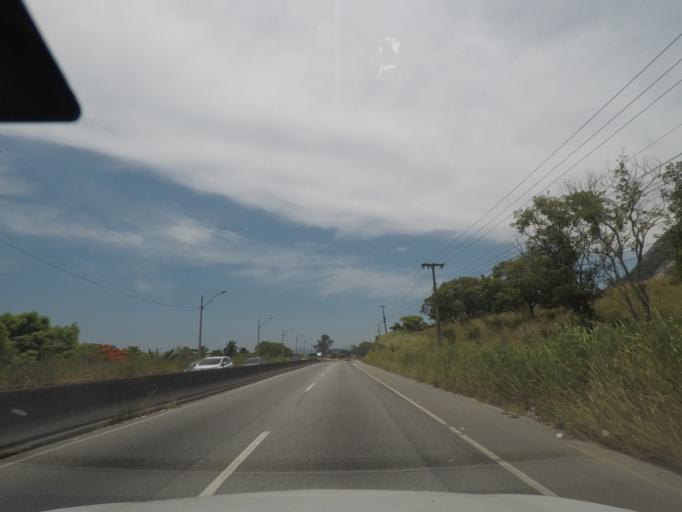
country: BR
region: Rio de Janeiro
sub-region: Marica
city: Marica
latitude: -22.9355
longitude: -42.9030
